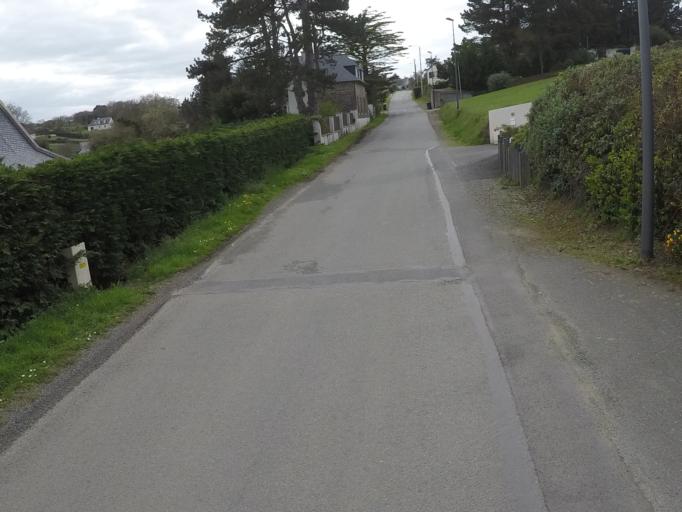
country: FR
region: Brittany
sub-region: Departement des Cotes-d'Armor
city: Plouezec
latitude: 48.7234
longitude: -2.9503
